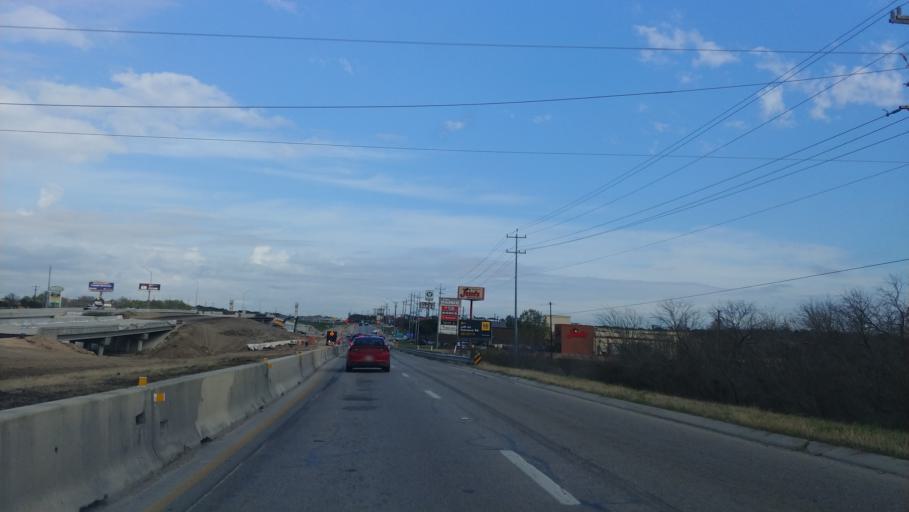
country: US
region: Texas
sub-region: Bexar County
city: Lackland Air Force Base
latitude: 29.4325
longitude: -98.7107
